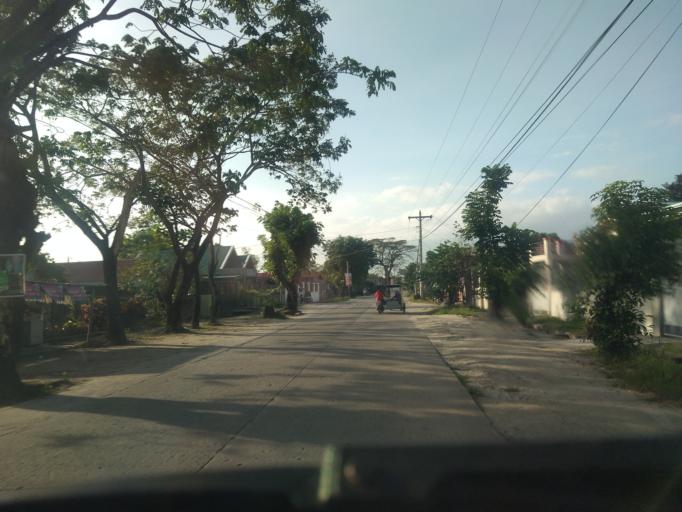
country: PH
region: Central Luzon
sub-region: Province of Pampanga
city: Bulaon
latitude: 15.0904
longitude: 120.6878
